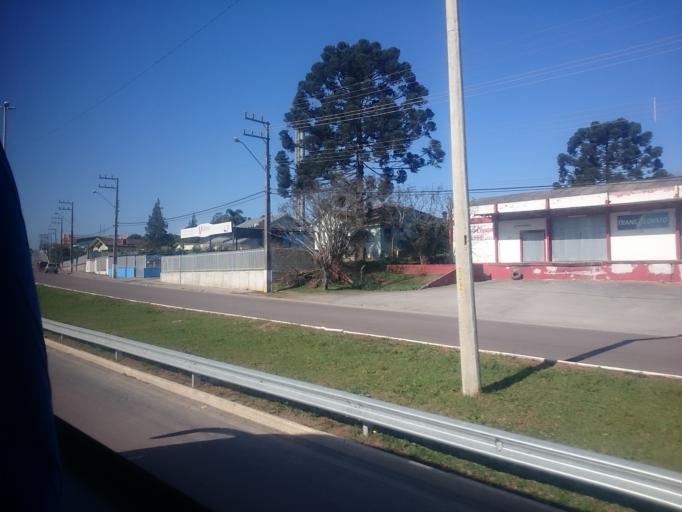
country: BR
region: Parana
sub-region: Rio Negro
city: Rio Negro
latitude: -26.0861
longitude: -49.7790
